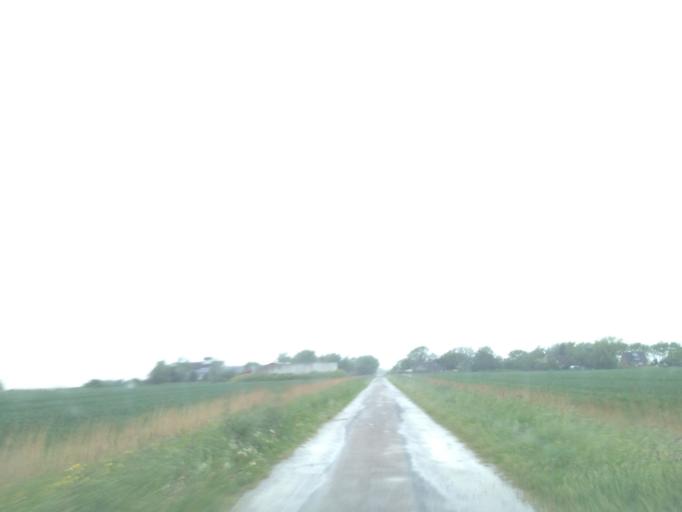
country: DE
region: Schleswig-Holstein
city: Klanxbull
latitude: 54.8844
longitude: 8.6913
